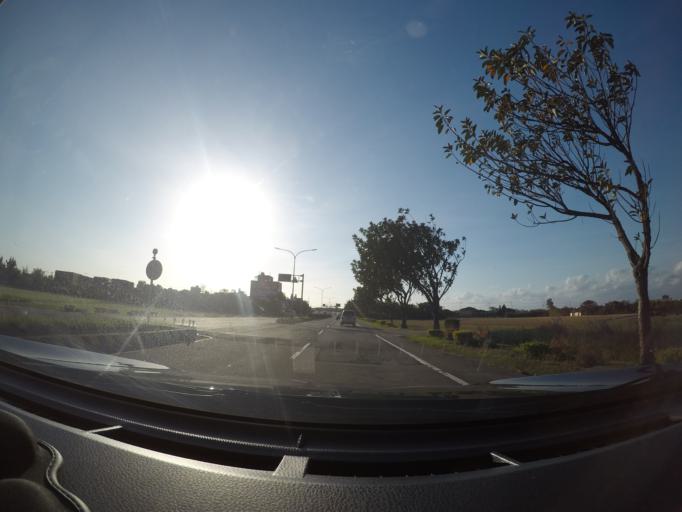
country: TW
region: Taiwan
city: Taoyuan City
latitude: 25.0799
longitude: 121.2127
